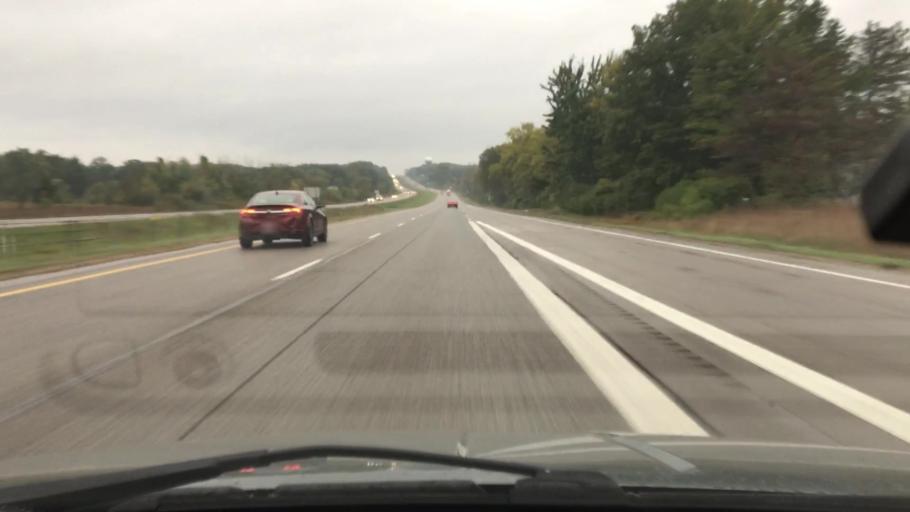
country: US
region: Michigan
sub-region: Washtenaw County
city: Chelsea
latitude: 42.2946
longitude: -84.0330
